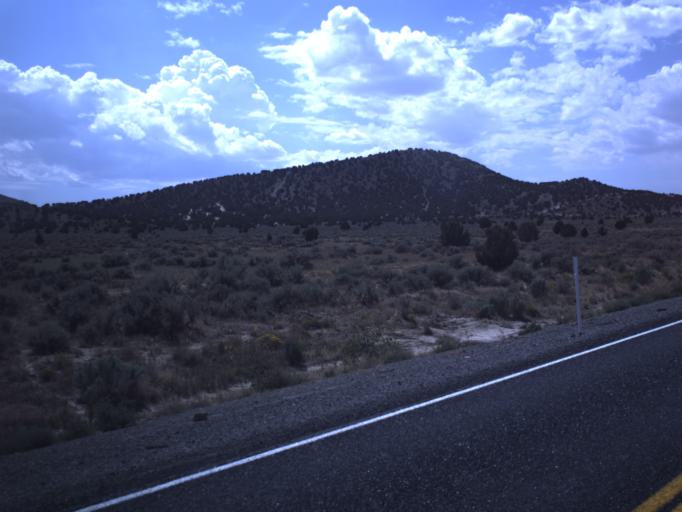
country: US
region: Utah
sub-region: Utah County
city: Eagle Mountain
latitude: 40.2350
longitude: -112.1673
